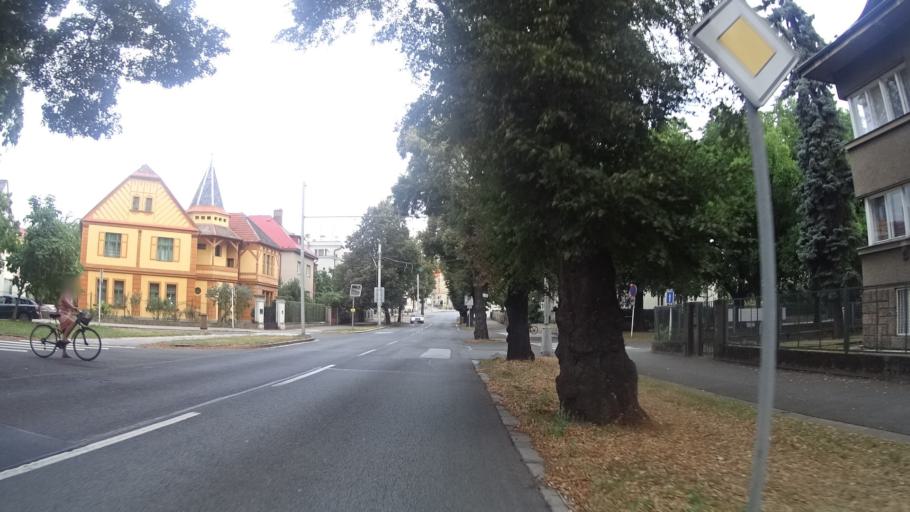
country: CZ
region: Kralovehradecky
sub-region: Okres Hradec Kralove
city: Hradec Kralove
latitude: 50.2090
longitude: 15.8396
